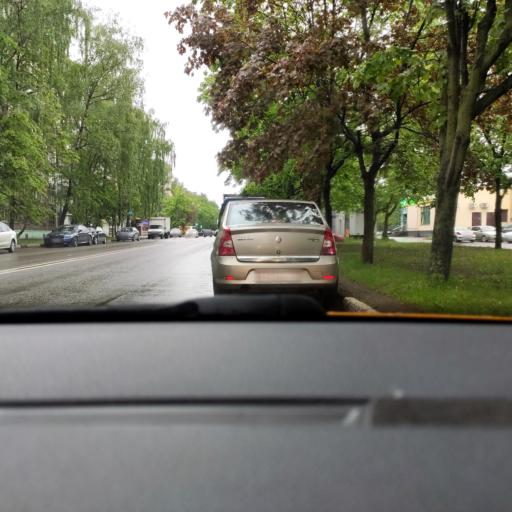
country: RU
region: Moskovskaya
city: Balashikha
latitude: 55.7928
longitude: 37.9710
